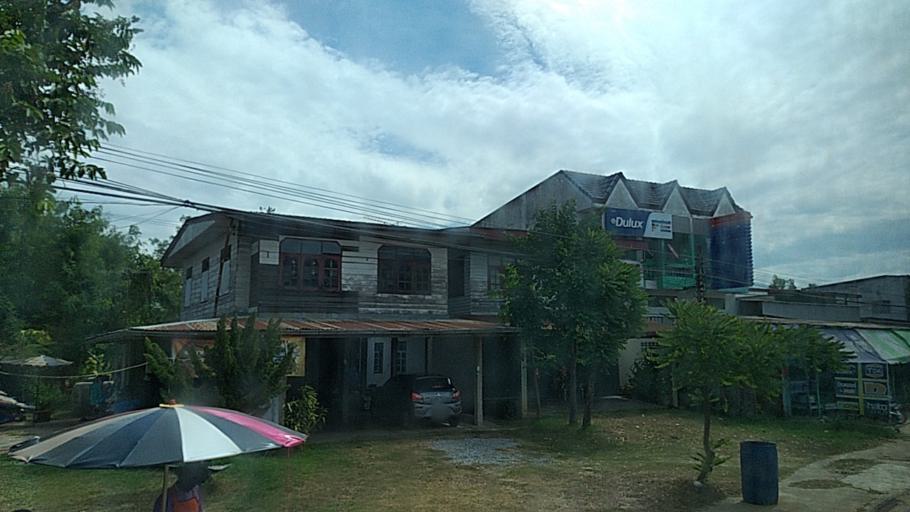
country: TH
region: Maha Sarakham
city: Chiang Yuen
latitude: 16.4057
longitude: 103.0987
